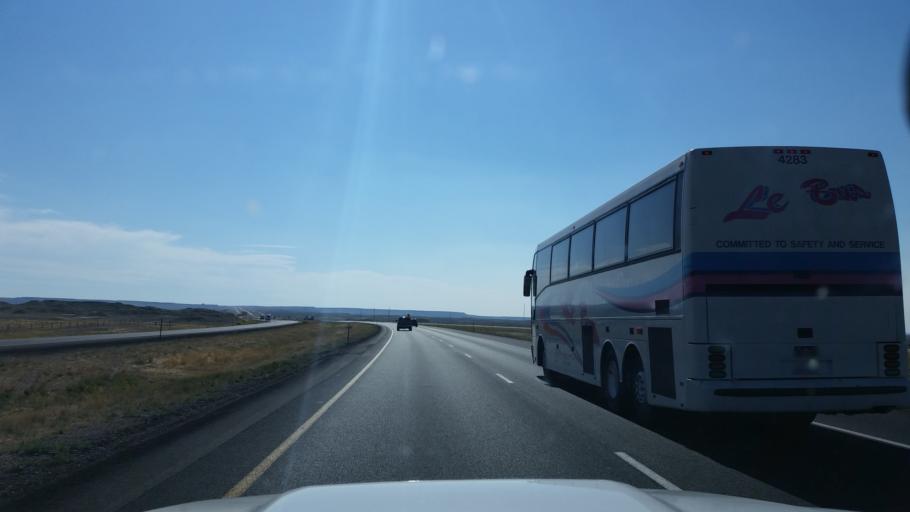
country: US
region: Wyoming
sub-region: Uinta County
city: Lyman
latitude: 41.5433
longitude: -109.9165
